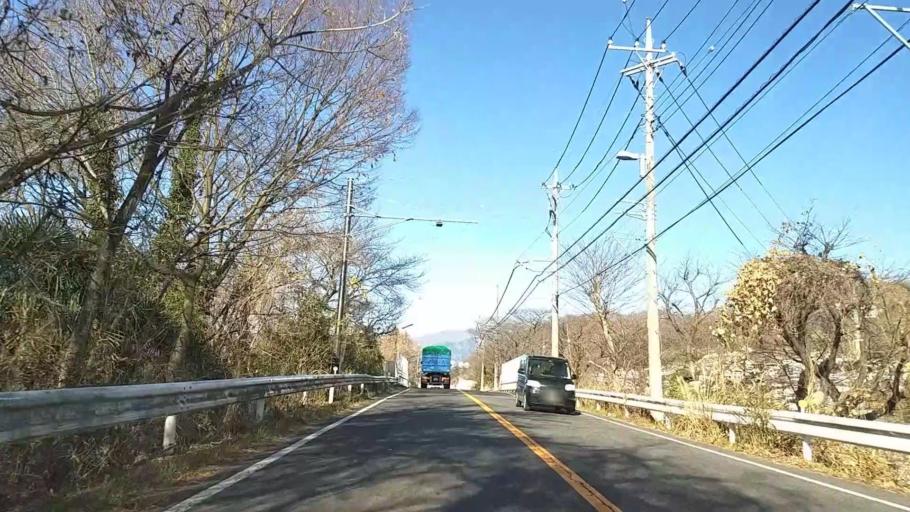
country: JP
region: Kanagawa
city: Hadano
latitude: 35.3628
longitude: 139.2469
